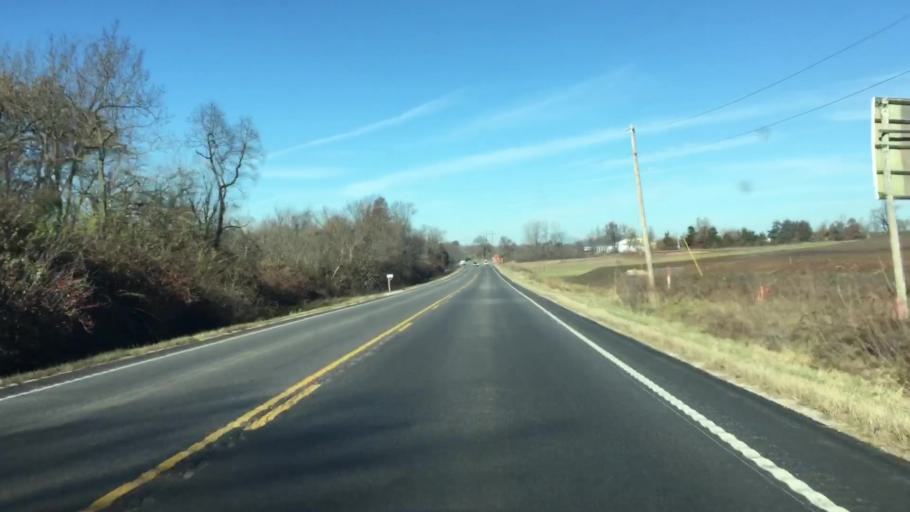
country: US
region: Missouri
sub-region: Miller County
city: Eldon
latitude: 38.3582
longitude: -92.6022
